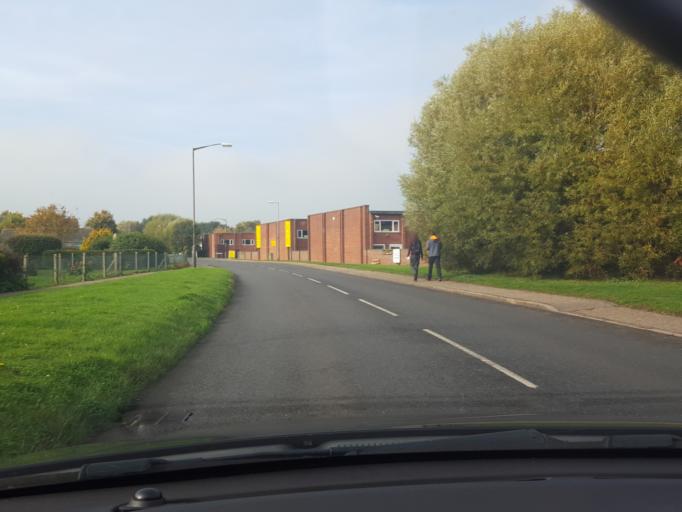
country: GB
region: England
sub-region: Essex
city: Manningtree
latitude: 51.9469
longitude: 1.0581
